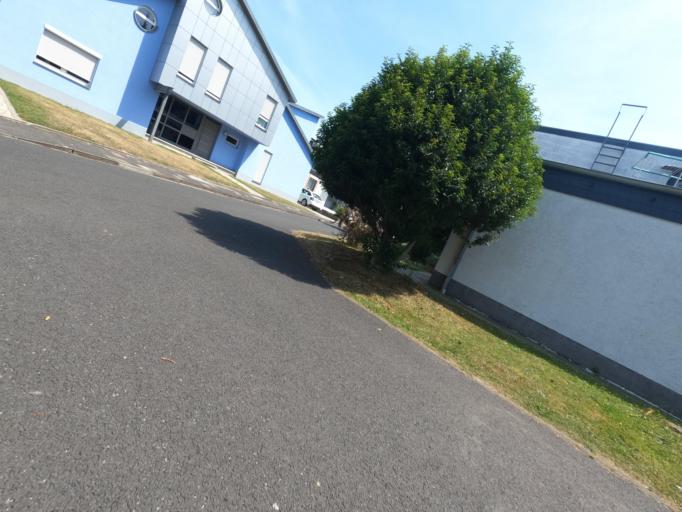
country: DE
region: North Rhine-Westphalia
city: Baesweiler
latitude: 50.9225
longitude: 6.1957
